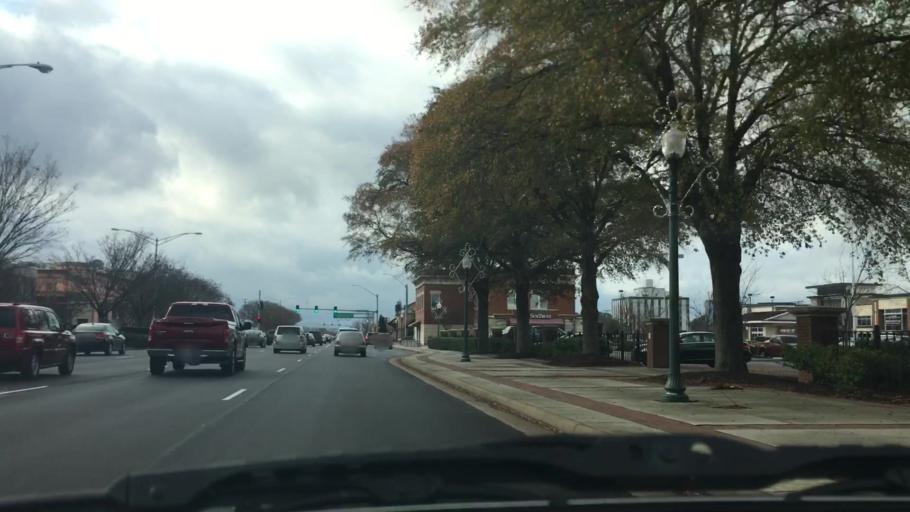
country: US
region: Virginia
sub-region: City of Chesapeake
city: Chesapeake
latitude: 36.8437
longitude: -76.1321
